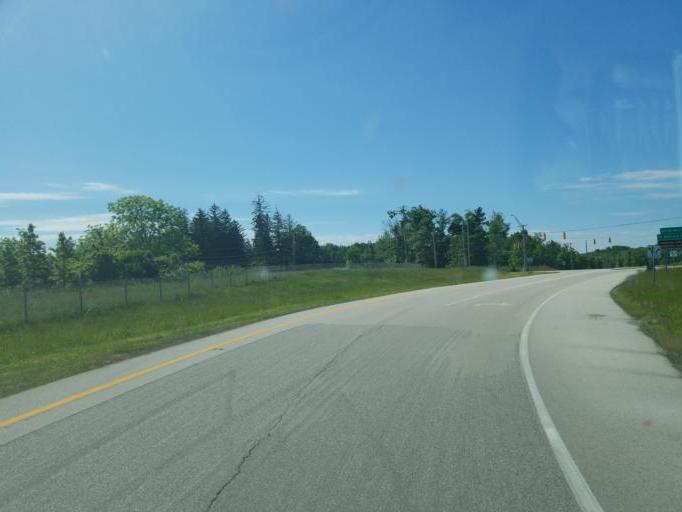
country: US
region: Ohio
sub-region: Summit County
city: Boston Heights
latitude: 41.2552
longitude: -81.4978
